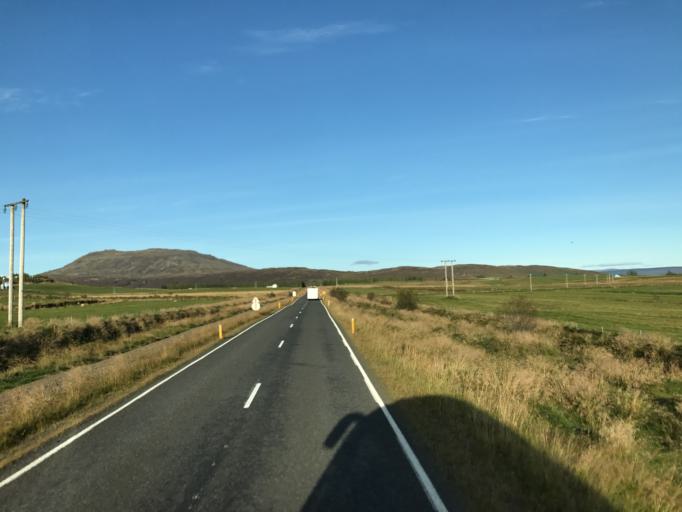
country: IS
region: South
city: Selfoss
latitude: 64.2691
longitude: -20.4569
